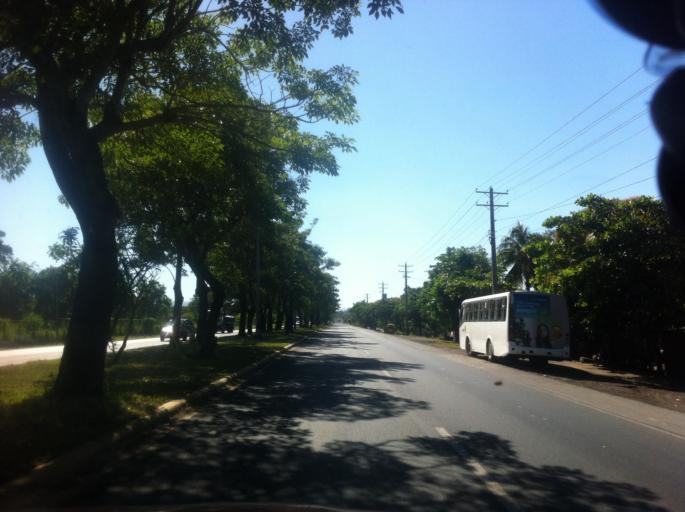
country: NI
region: Managua
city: Tipitapa
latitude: 12.1537
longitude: -86.1480
